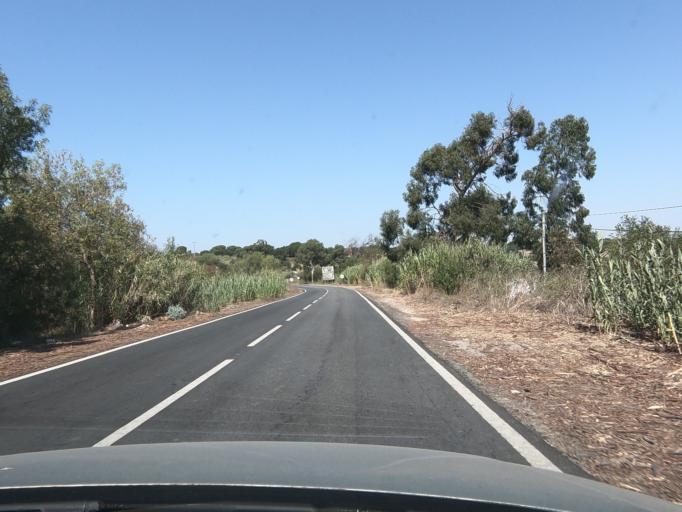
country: PT
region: Setubal
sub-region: Alcacer do Sal
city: Alcacer do Sal
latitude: 38.3652
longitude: -8.4859
